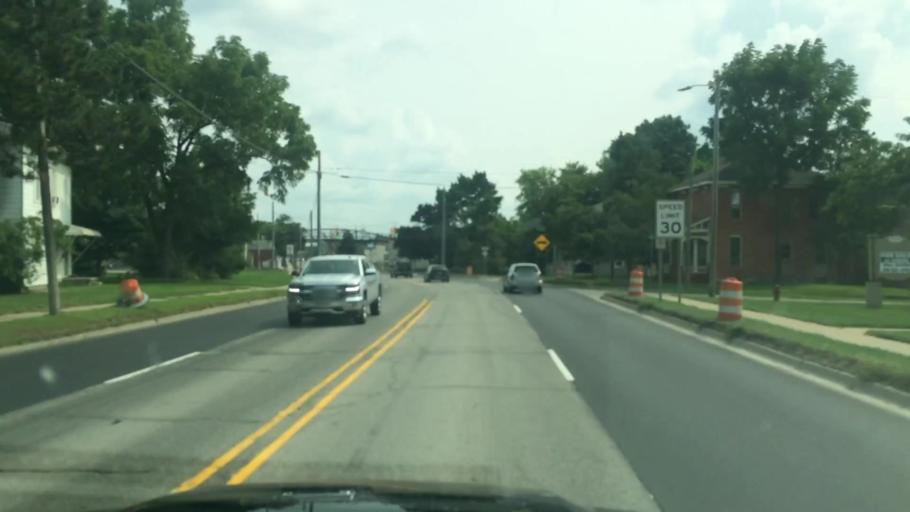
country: US
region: Michigan
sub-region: Oakland County
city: Oxford
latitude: 42.8289
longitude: -83.2686
